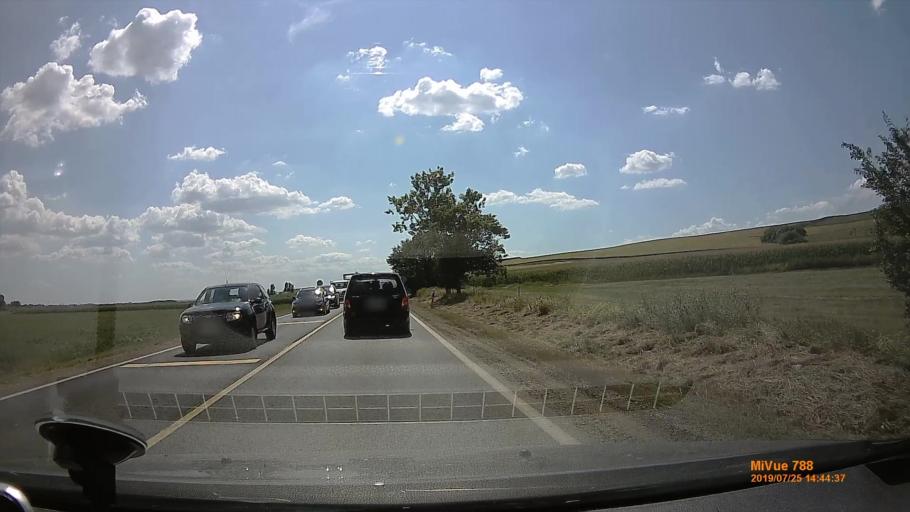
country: HU
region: Borsod-Abauj-Zemplen
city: Halmaj
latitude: 48.2669
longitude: 20.9994
